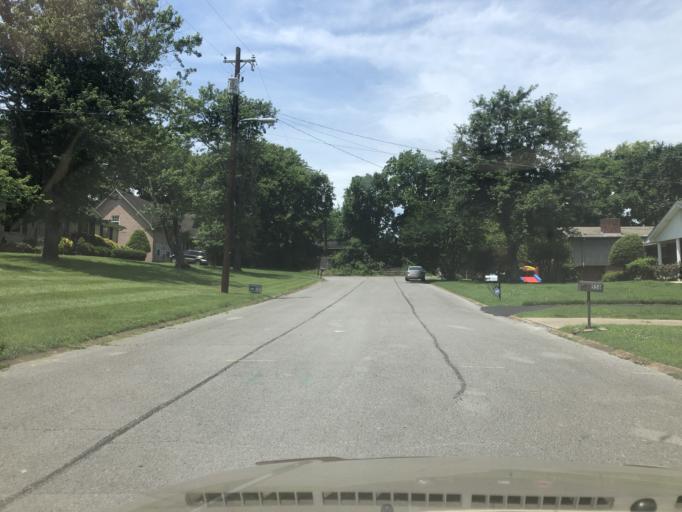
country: US
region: Tennessee
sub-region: Davidson County
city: Lakewood
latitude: 36.2482
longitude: -86.6758
